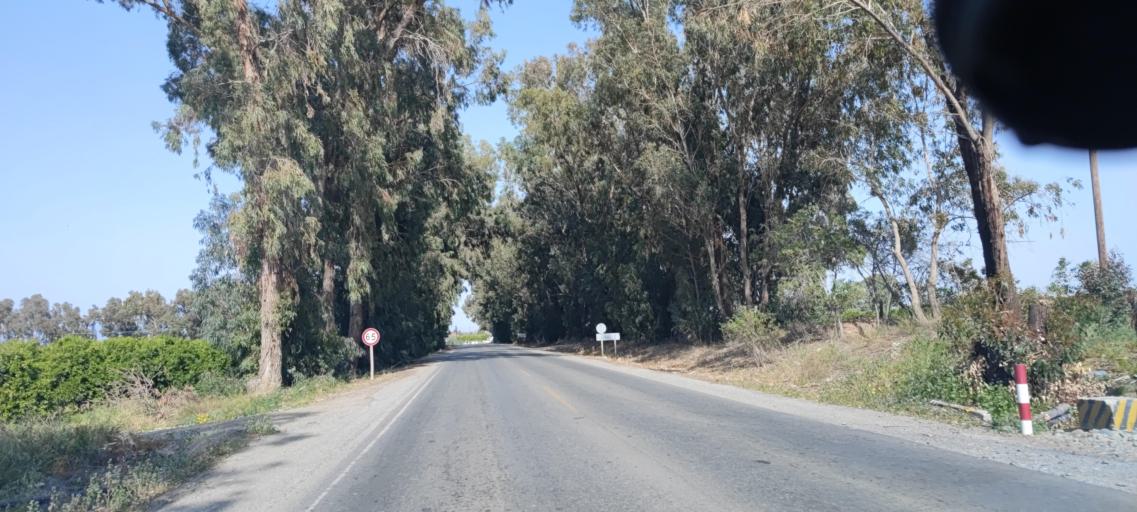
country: CY
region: Lefkosia
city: Lefka
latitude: 35.1567
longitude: 32.8922
